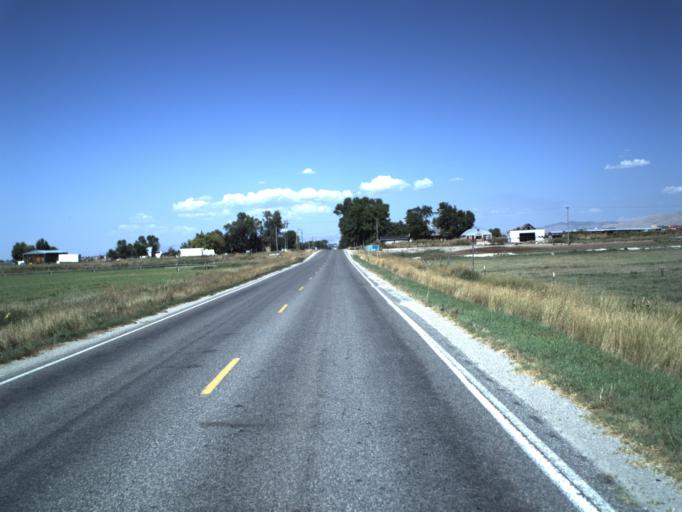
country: US
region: Utah
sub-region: Cache County
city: Lewiston
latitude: 42.0004
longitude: -111.8766
